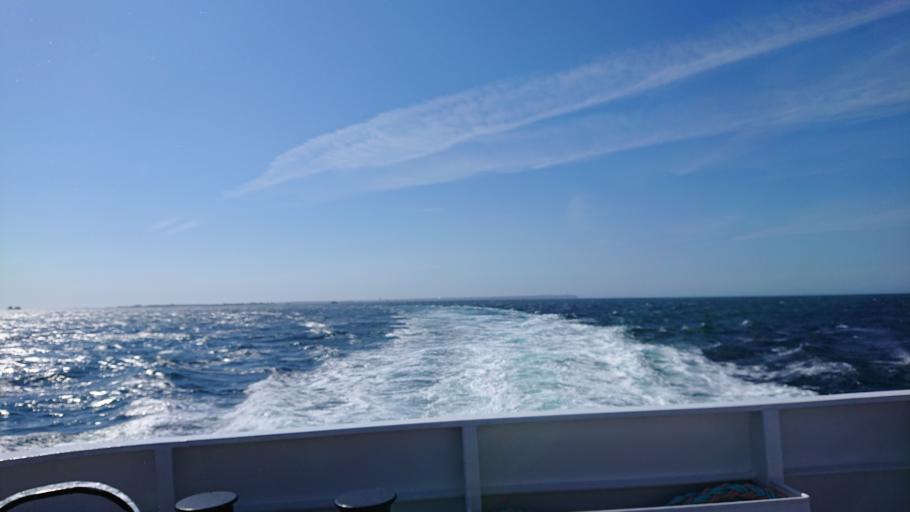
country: FR
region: Brittany
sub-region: Departement du Finistere
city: Le Conquet
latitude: 48.4140
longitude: -4.9385
